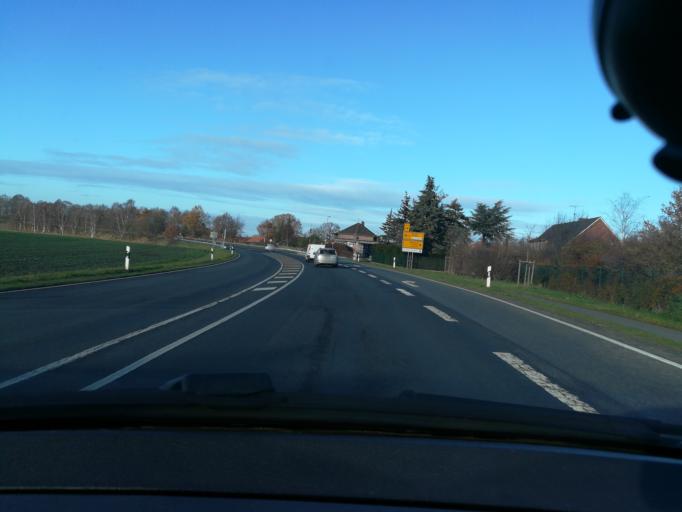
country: DE
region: Lower Saxony
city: Kirchdorf
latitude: 52.5892
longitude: 8.8384
